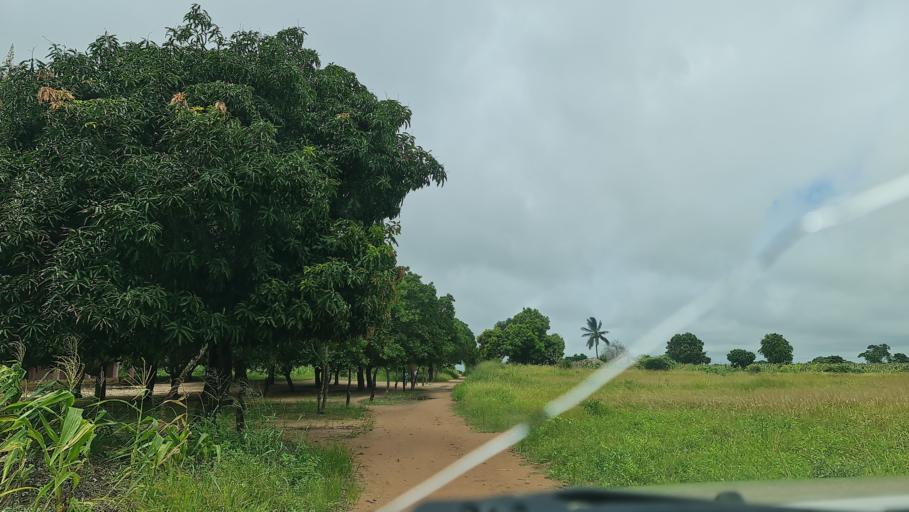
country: MW
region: Southern Region
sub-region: Nsanje District
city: Nsanje
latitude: -17.3364
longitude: 35.7183
